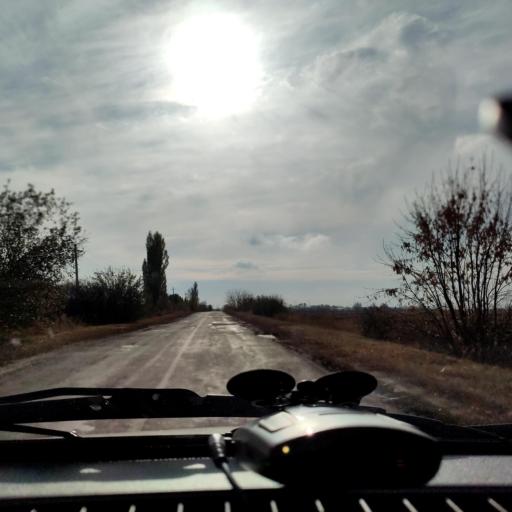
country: RU
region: Voronezj
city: Rossosh'
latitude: 51.2240
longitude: 38.7614
